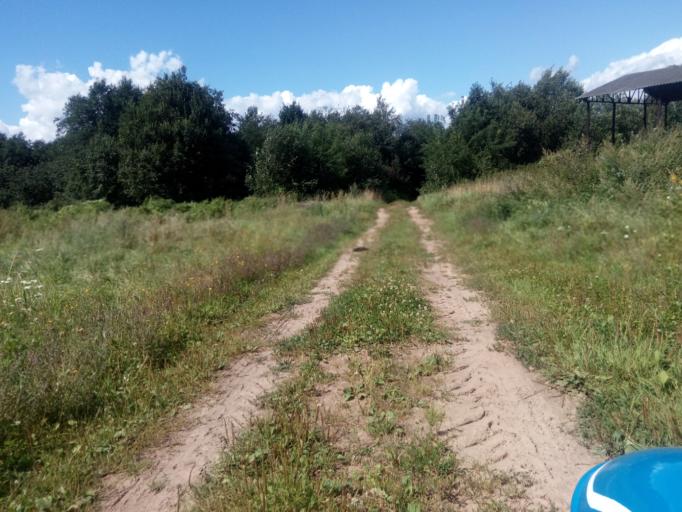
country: BY
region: Vitebsk
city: Dzisna
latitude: 55.6764
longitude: 28.3198
